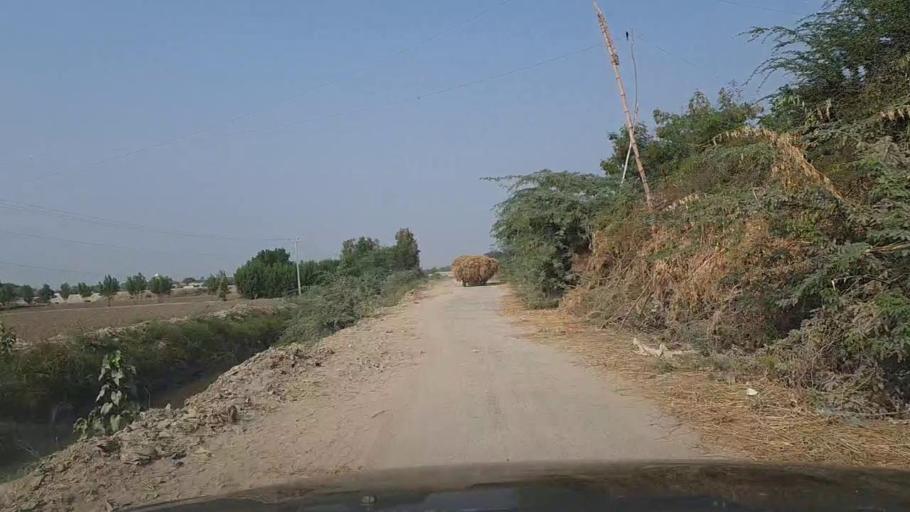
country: PK
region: Sindh
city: Mirpur Batoro
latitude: 24.7120
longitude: 68.2546
